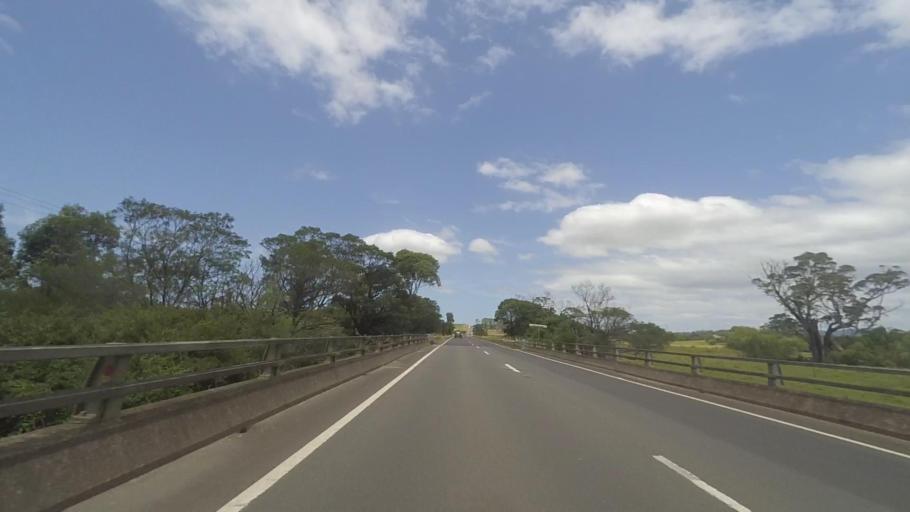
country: AU
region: New South Wales
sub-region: Shoalhaven Shire
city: Milton
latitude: -35.2746
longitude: 150.4237
